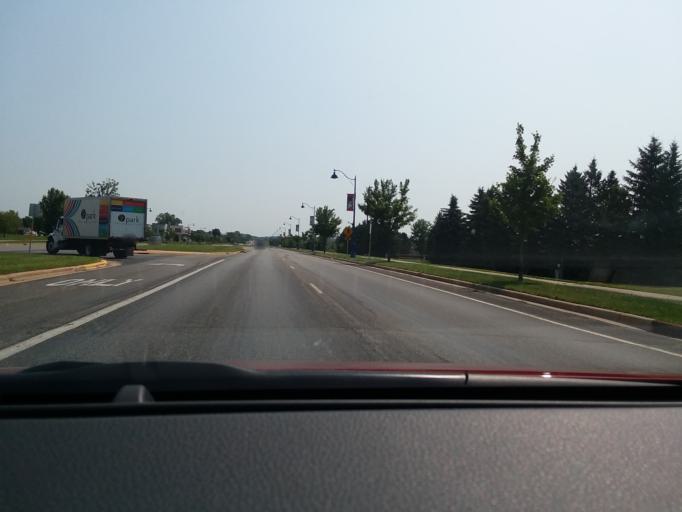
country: US
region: Wisconsin
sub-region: Dane County
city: Verona
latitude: 42.9930
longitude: -89.5246
